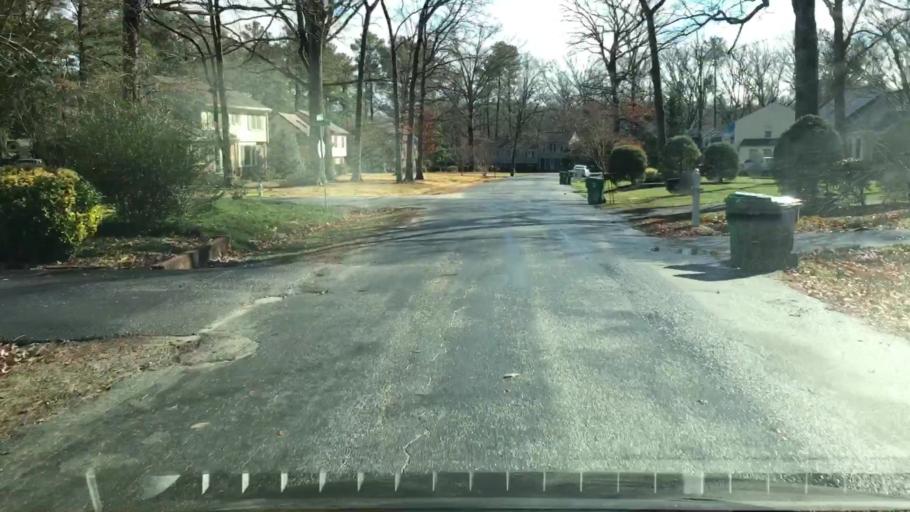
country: US
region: Virginia
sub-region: Chesterfield County
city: Bon Air
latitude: 37.5272
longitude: -77.5982
